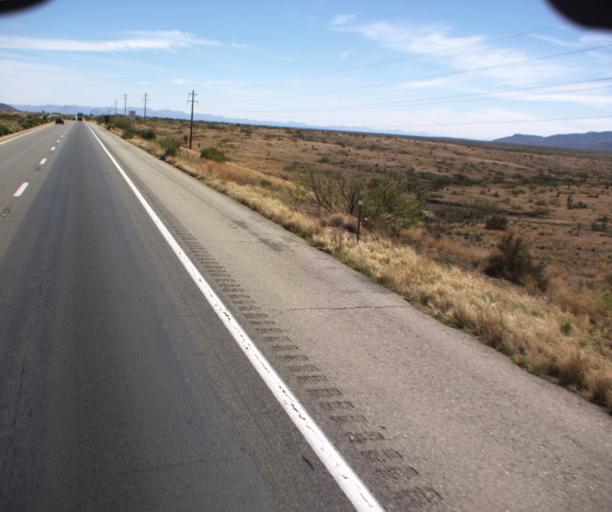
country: US
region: Arizona
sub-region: Cochise County
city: Willcox
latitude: 32.3602
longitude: -109.6683
